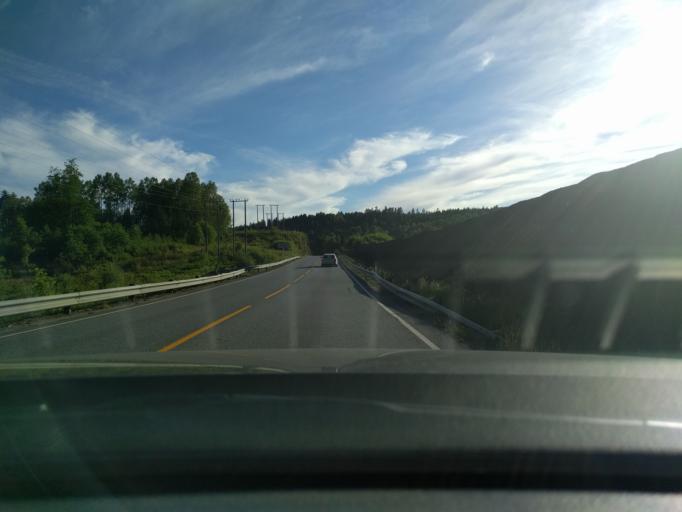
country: NO
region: Vestfold
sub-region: Hof
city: Hof
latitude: 59.5116
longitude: 10.0906
